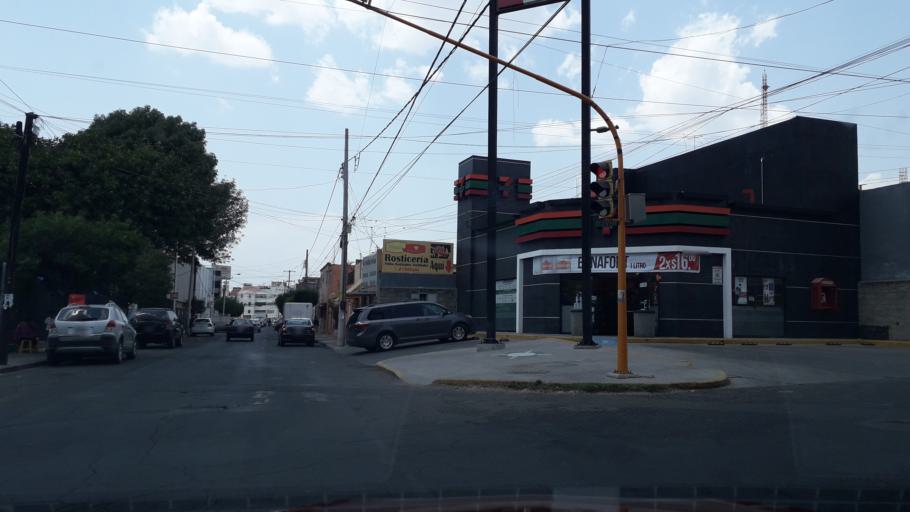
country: MX
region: Puebla
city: Puebla
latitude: 19.0374
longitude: -98.2179
